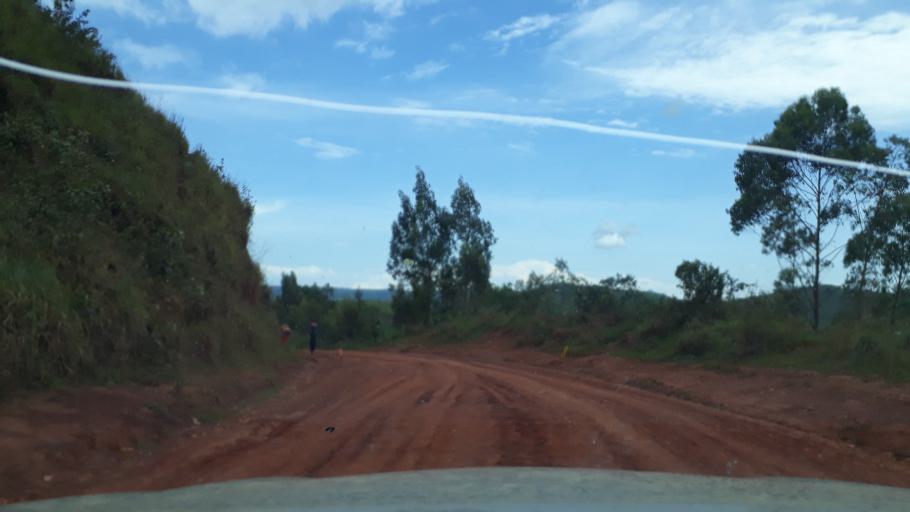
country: CD
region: Eastern Province
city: Bunia
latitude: 1.7562
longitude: 30.3692
